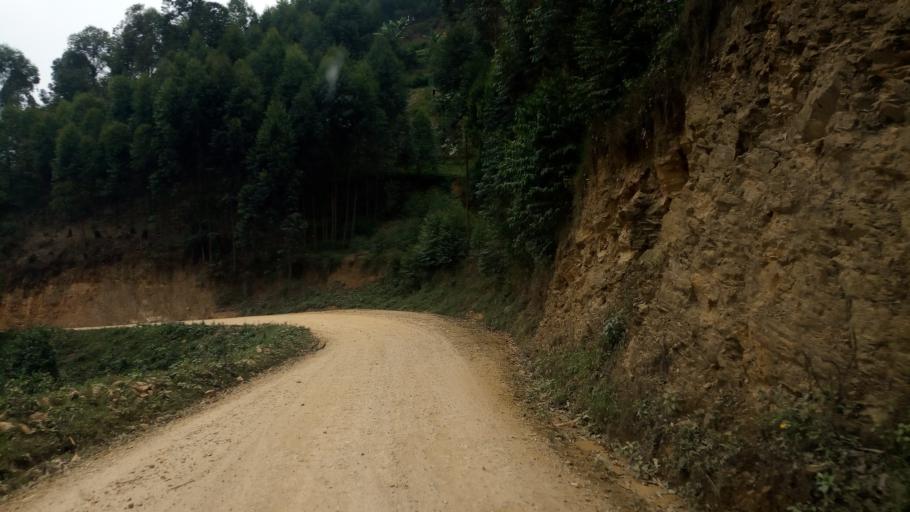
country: UG
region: Western Region
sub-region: Kanungu District
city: Kanungu
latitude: -1.1107
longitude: 29.8685
